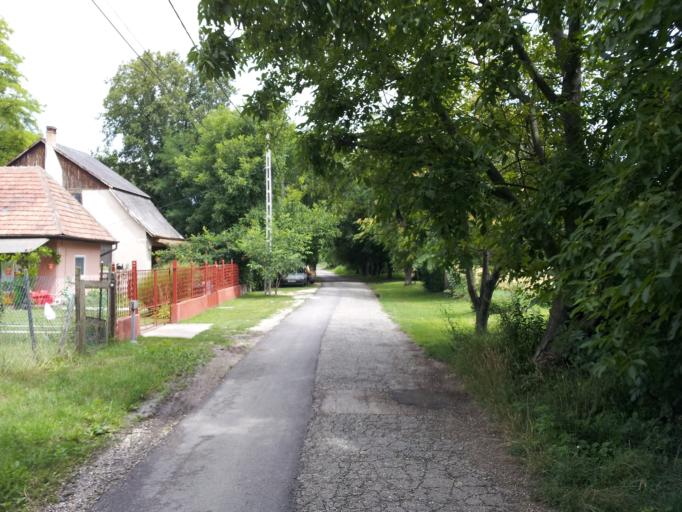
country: HU
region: Pest
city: Szigetujfalu
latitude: 47.2166
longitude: 18.9678
